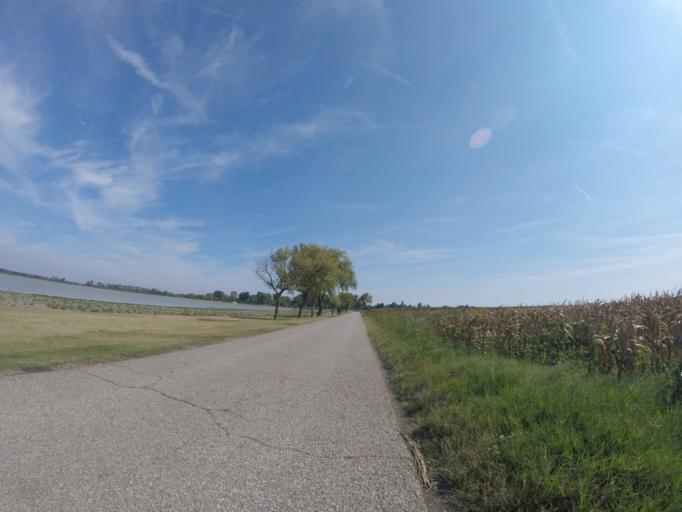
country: AT
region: Burgenland
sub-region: Politischer Bezirk Neusiedl am See
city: Sankt Andra am Zicksee
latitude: 47.7849
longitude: 16.9064
